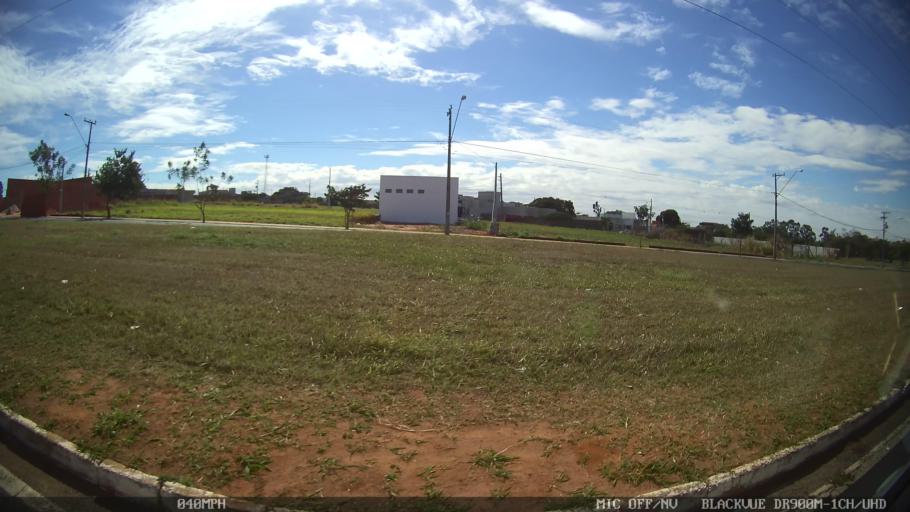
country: BR
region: Sao Paulo
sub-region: Sao Jose Do Rio Preto
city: Sao Jose do Rio Preto
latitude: -20.8171
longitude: -49.4862
